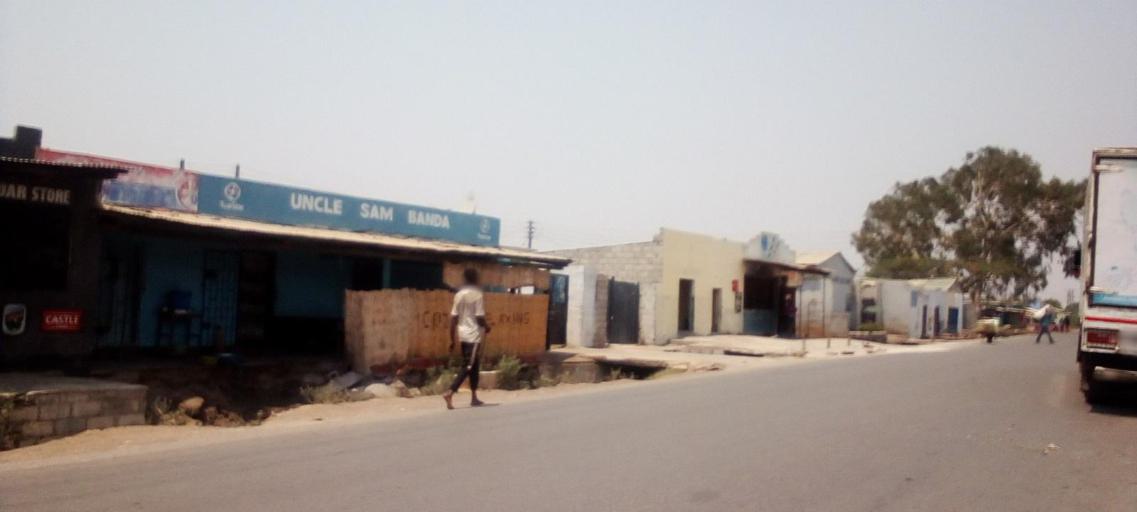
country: ZM
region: Lusaka
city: Lusaka
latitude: -15.4395
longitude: 28.2542
